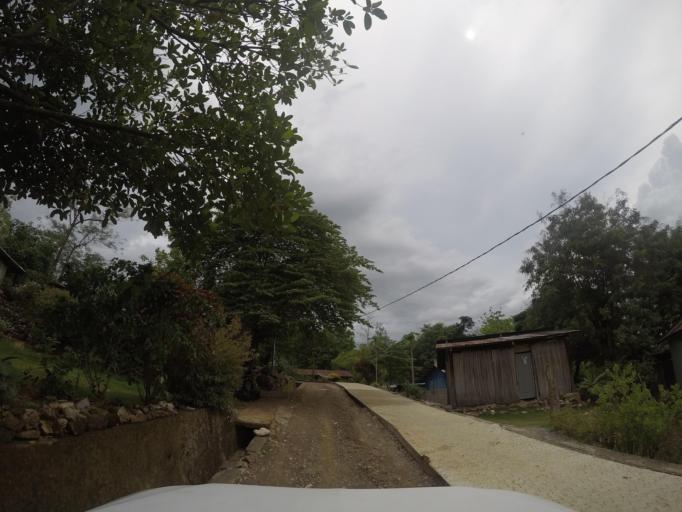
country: TL
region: Bobonaro
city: Maliana
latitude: -8.9949
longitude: 125.2150
